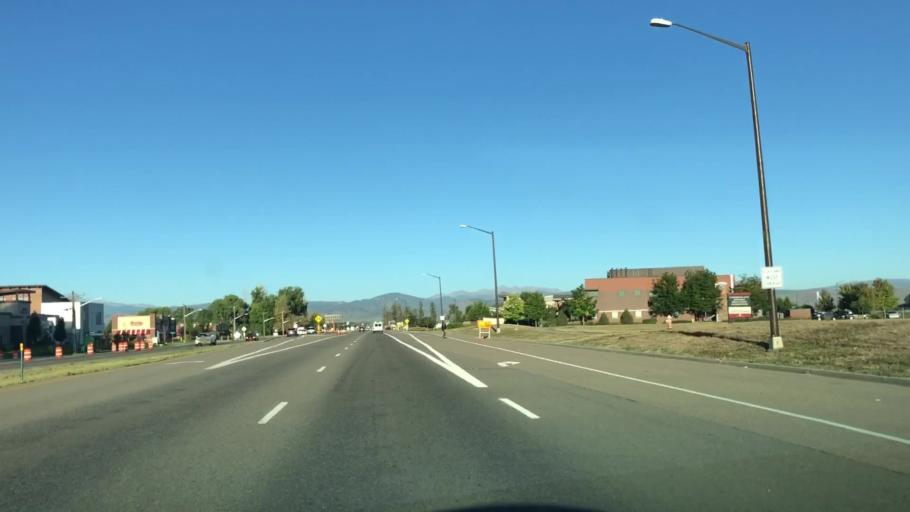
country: US
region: Colorado
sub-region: Larimer County
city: Loveland
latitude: 40.4032
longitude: -105.0252
